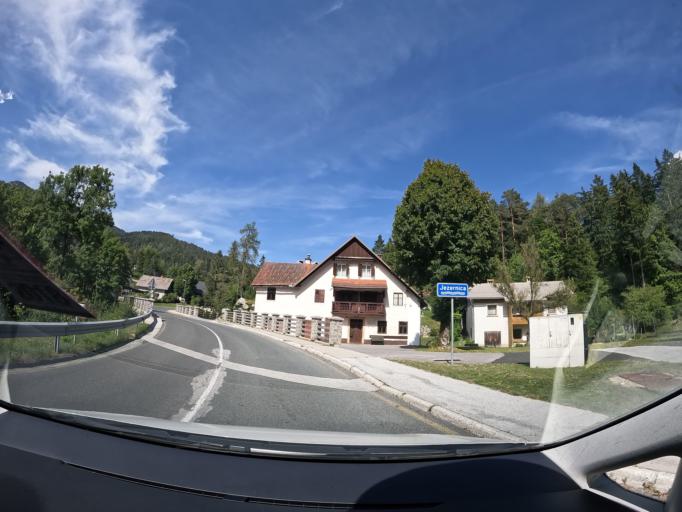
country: AT
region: Carinthia
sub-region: Politischer Bezirk Klagenfurt Land
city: Moosburg
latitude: 46.6566
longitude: 14.1357
